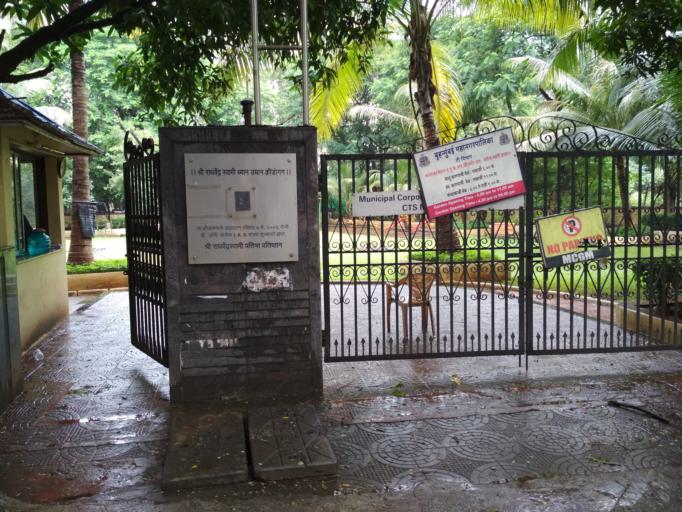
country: IN
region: Maharashtra
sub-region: Thane
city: Thane
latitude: 19.1635
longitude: 72.9419
